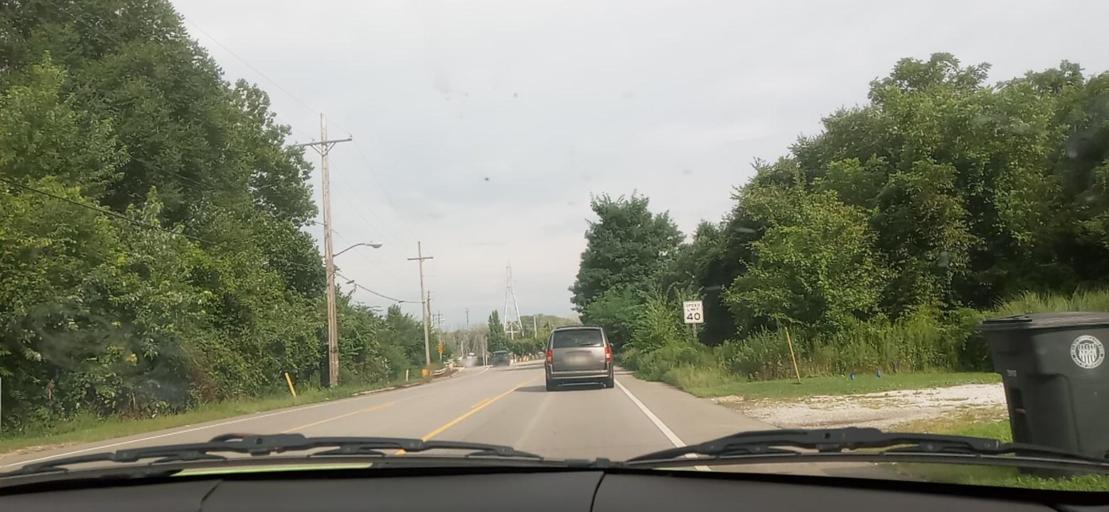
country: US
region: Ohio
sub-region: Summit County
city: Portage Lakes
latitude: 41.0290
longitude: -81.5399
